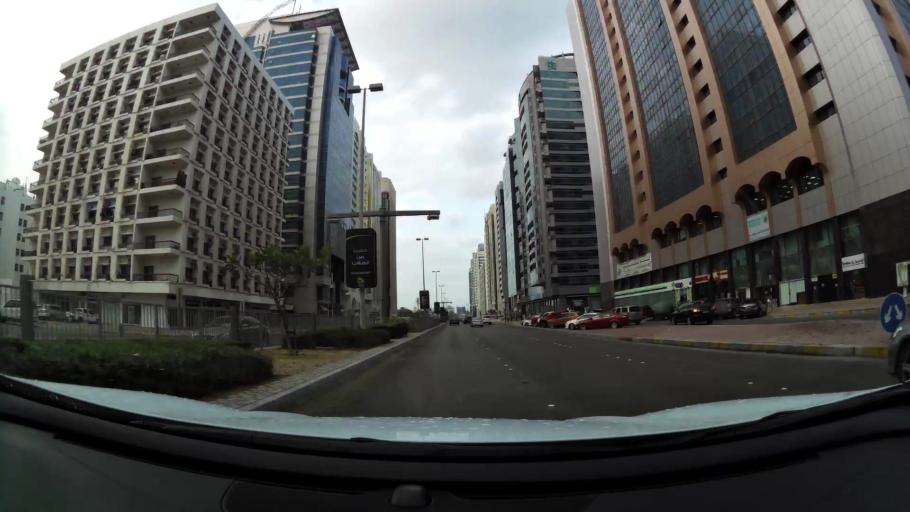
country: AE
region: Abu Dhabi
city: Abu Dhabi
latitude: 24.4728
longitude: 54.3470
